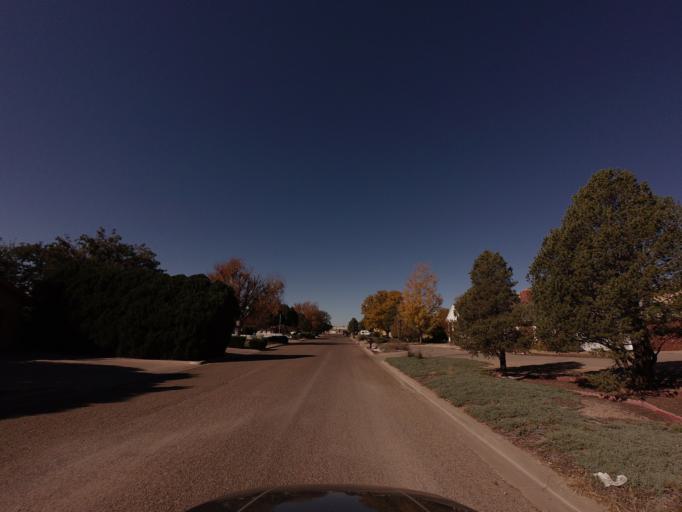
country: US
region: New Mexico
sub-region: Curry County
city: Clovis
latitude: 34.4234
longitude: -103.1904
